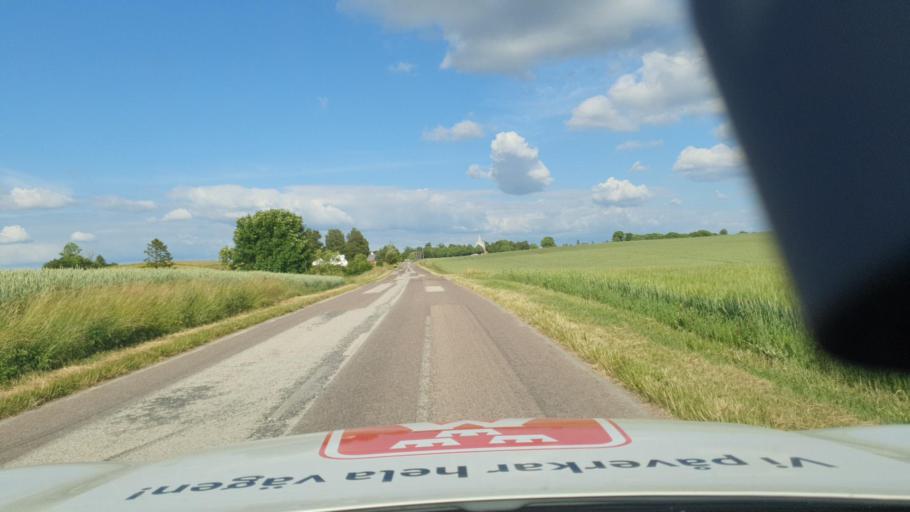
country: SE
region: Skane
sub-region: Skurups Kommun
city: Rydsgard
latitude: 55.4334
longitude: 13.6039
